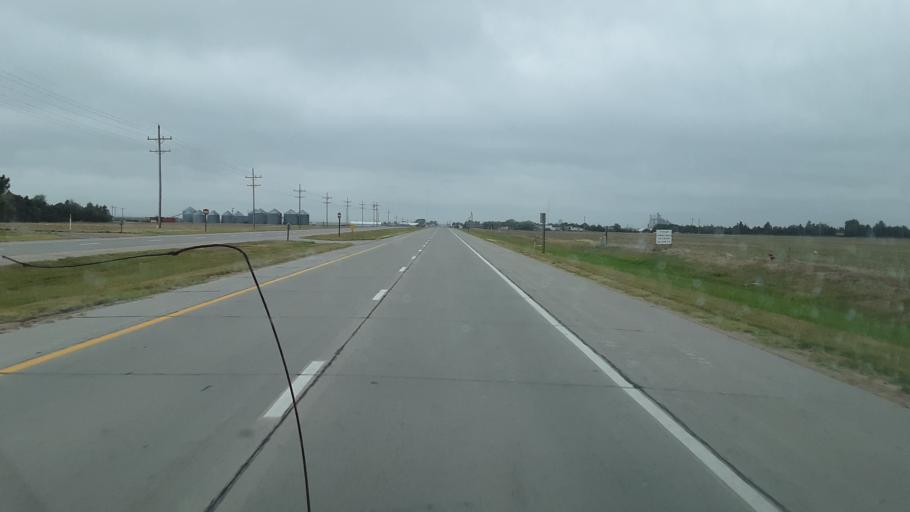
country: US
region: Kansas
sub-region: Logan County
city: Oakley
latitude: 39.1195
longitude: -100.8249
